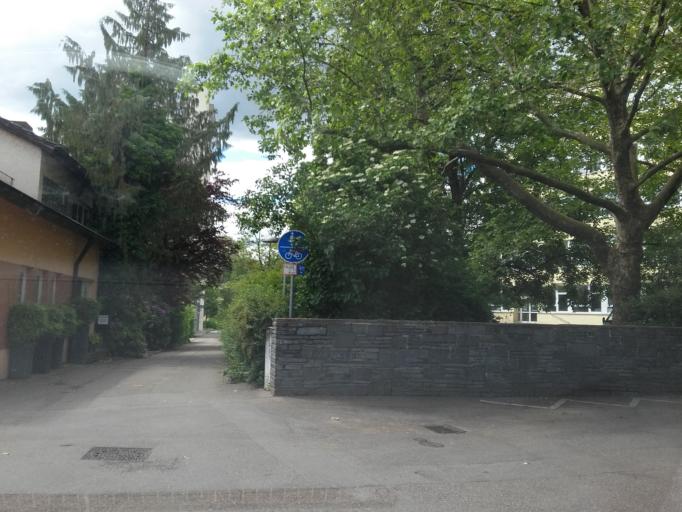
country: DE
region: Baden-Wuerttemberg
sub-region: Regierungsbezirk Stuttgart
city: Esslingen
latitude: 48.7316
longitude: 9.3393
